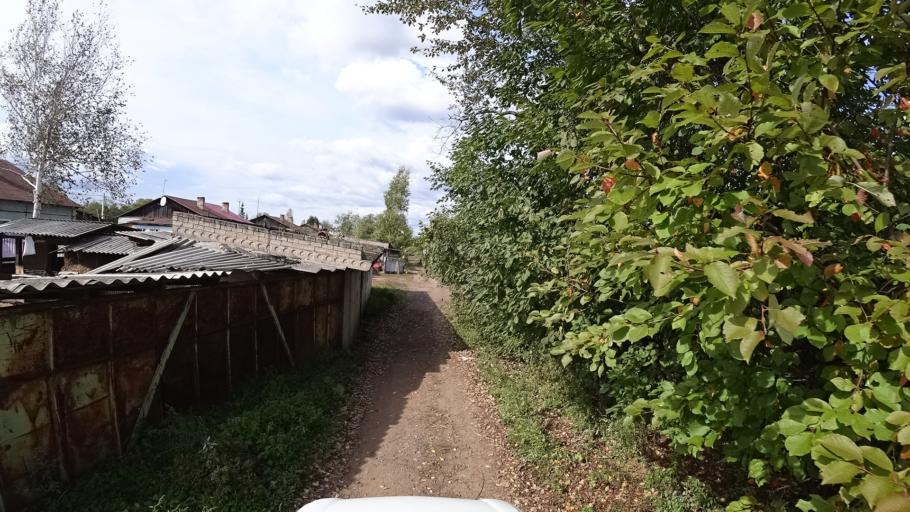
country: RU
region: Amur
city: Arkhara
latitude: 49.3526
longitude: 130.1593
